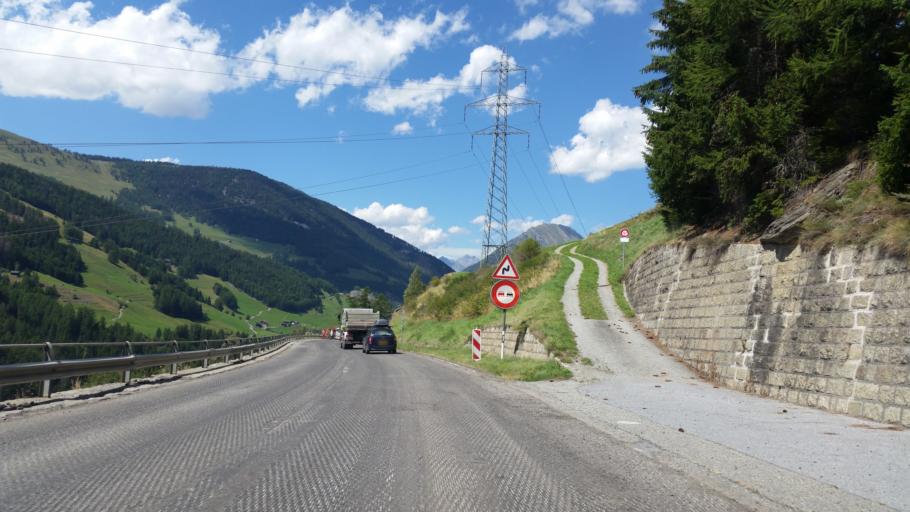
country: CH
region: Valais
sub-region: Entremont District
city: Orsieres
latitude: 45.9789
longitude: 7.1991
